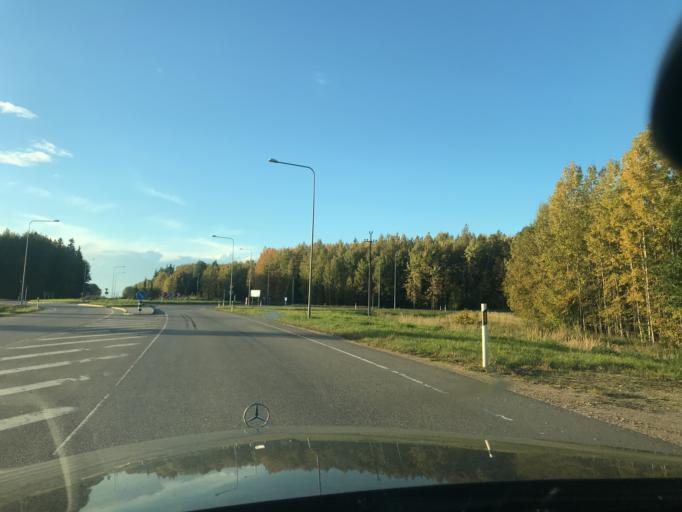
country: EE
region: Vorumaa
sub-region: Voru linn
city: Voru
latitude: 57.8486
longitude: 27.0400
